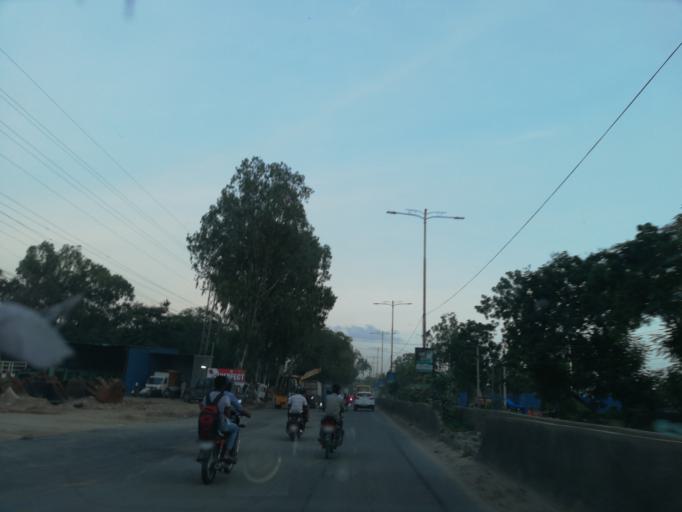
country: IN
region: Telangana
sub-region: Medak
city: Serilingampalle
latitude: 17.5245
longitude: 78.3555
